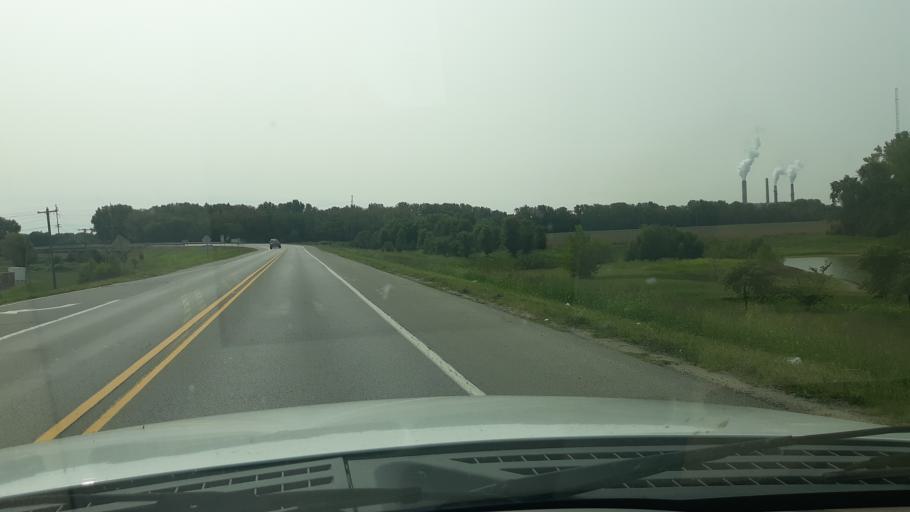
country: US
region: Illinois
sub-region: Wabash County
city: Mount Carmel
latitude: 38.4028
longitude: -87.7608
